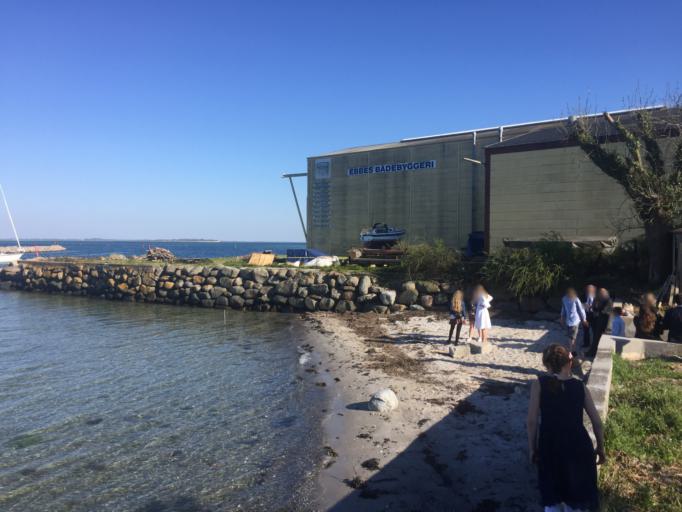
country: DK
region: South Denmark
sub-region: AEro Kommune
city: Marstal
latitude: 54.8579
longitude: 10.5204
